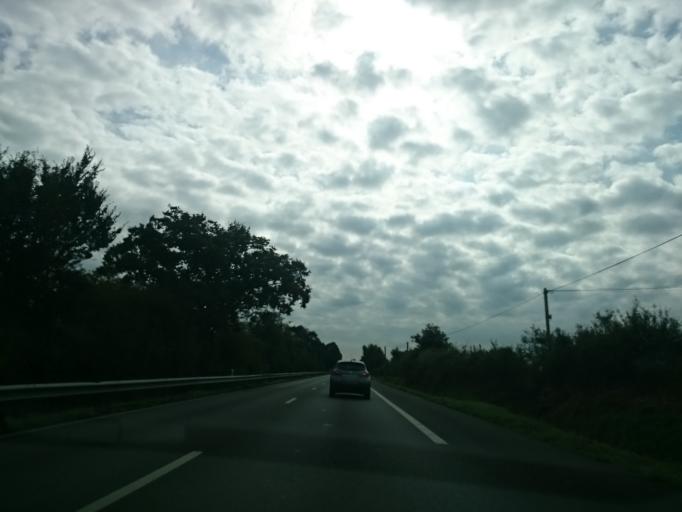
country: FR
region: Pays de la Loire
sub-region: Departement de la Loire-Atlantique
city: Vigneux-de-Bretagne
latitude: 47.2954
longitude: -1.7477
